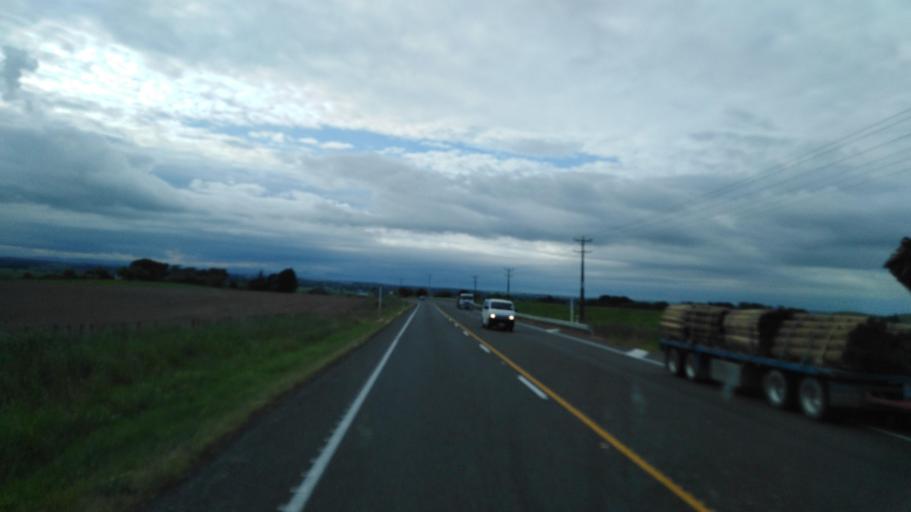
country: NZ
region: Manawatu-Wanganui
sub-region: Rangitikei District
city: Bulls
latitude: -40.1429
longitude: 175.3690
